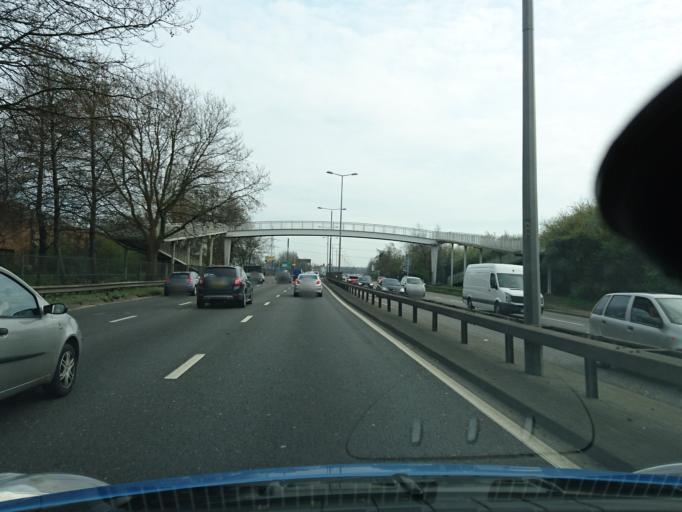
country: GB
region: England
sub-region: Greater London
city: Walthamstow
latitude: 51.6066
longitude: -0.0273
